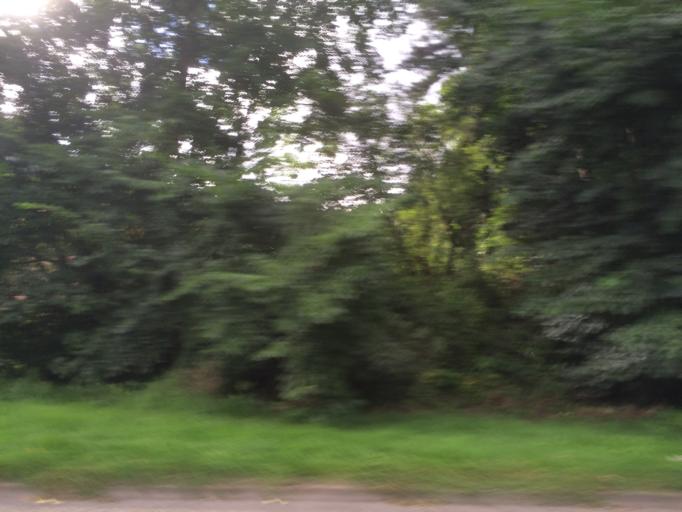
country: GB
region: Scotland
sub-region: Perth and Kinross
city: Perth
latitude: 56.4081
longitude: -3.4605
